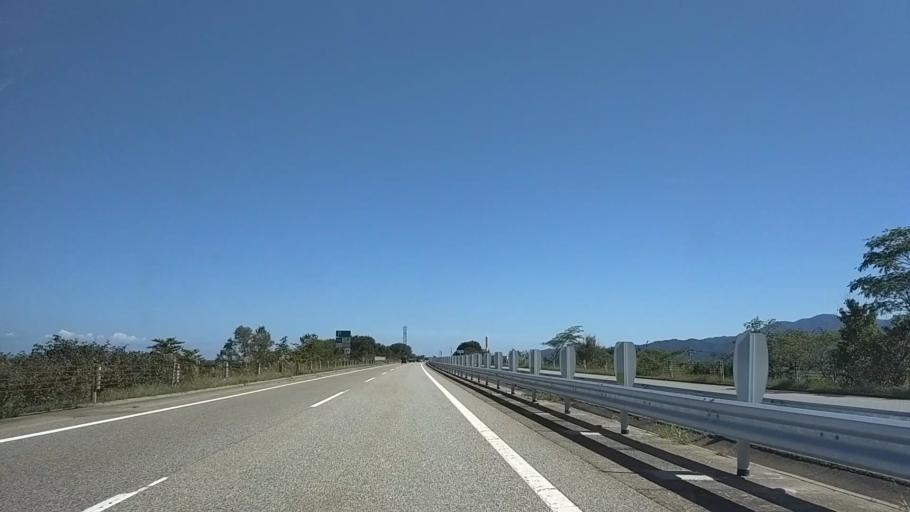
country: JP
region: Toyama
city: Nyuzen
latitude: 36.9072
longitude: 137.5046
